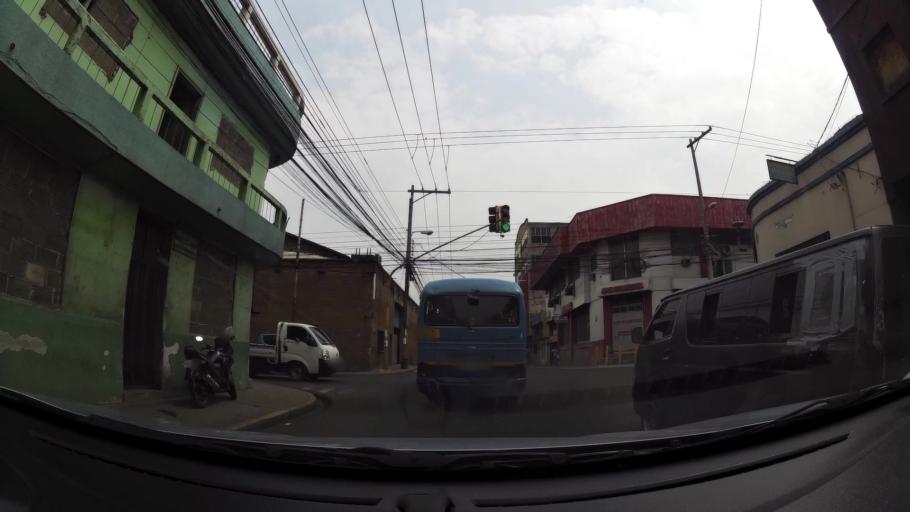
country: HN
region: Francisco Morazan
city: Tegucigalpa
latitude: 14.0963
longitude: -87.2076
